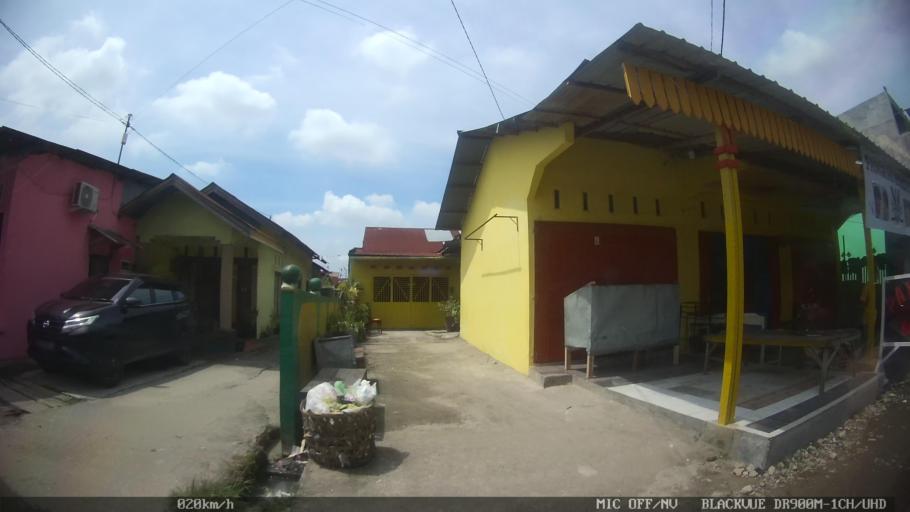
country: ID
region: North Sumatra
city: Medan
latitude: 3.6513
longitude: 98.6897
